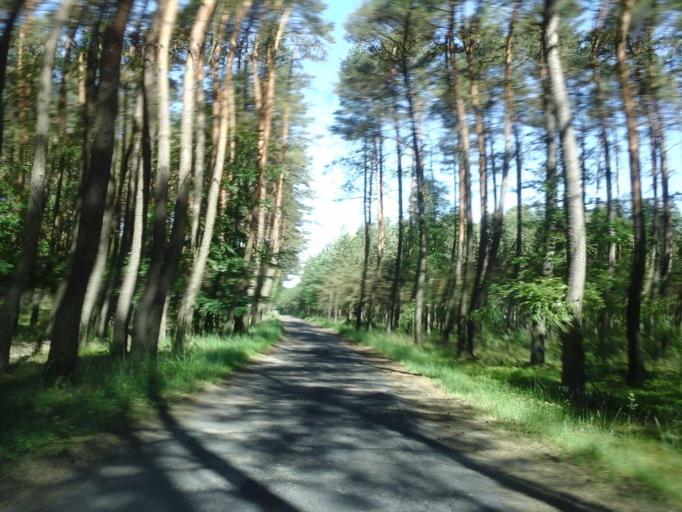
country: PL
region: West Pomeranian Voivodeship
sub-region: Powiat drawski
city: Kalisz Pomorski
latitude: 53.1245
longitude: 15.9084
